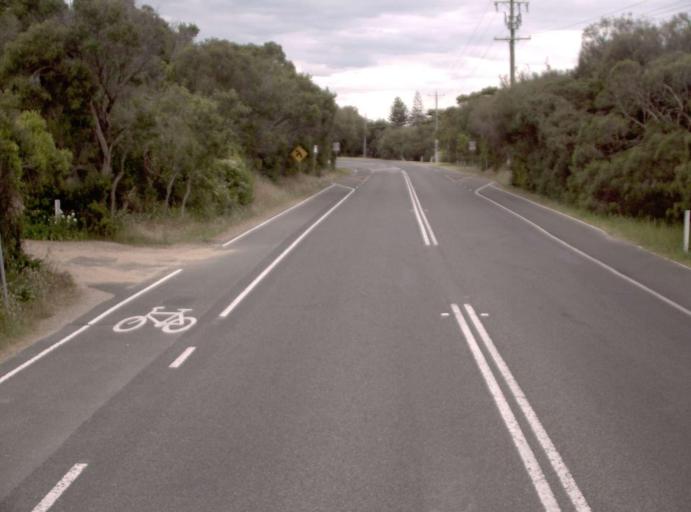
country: AU
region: Victoria
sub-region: Mornington Peninsula
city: Blairgowrie
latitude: -38.3508
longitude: 144.7618
